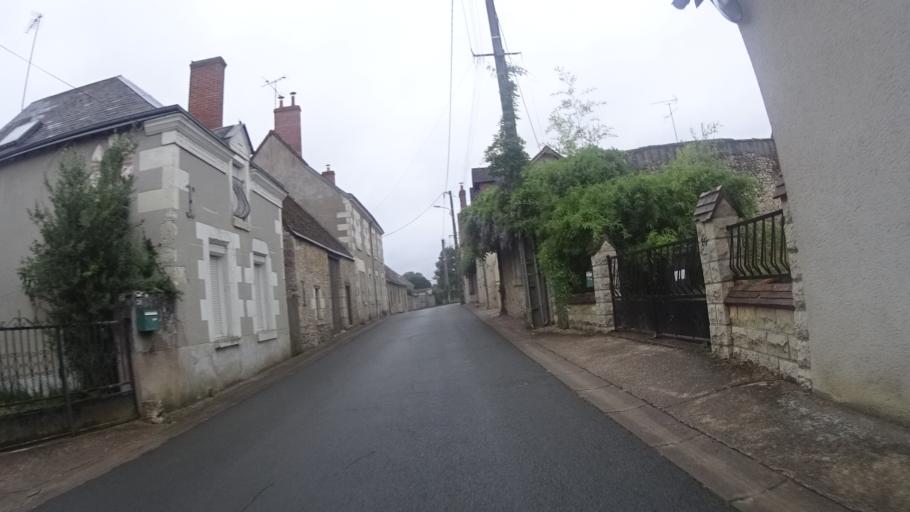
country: FR
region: Centre
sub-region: Departement du Loir-et-Cher
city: Cande-sur-Beuvron
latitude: 47.4947
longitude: 1.2581
